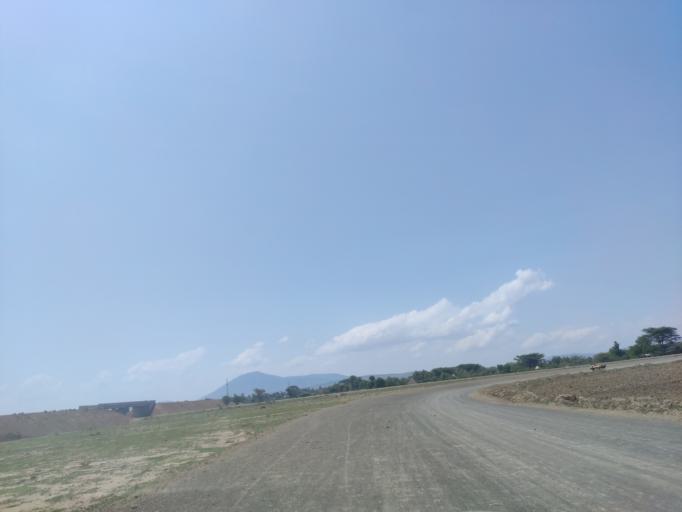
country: ET
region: Oromiya
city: Mojo
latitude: 8.3022
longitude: 38.9335
